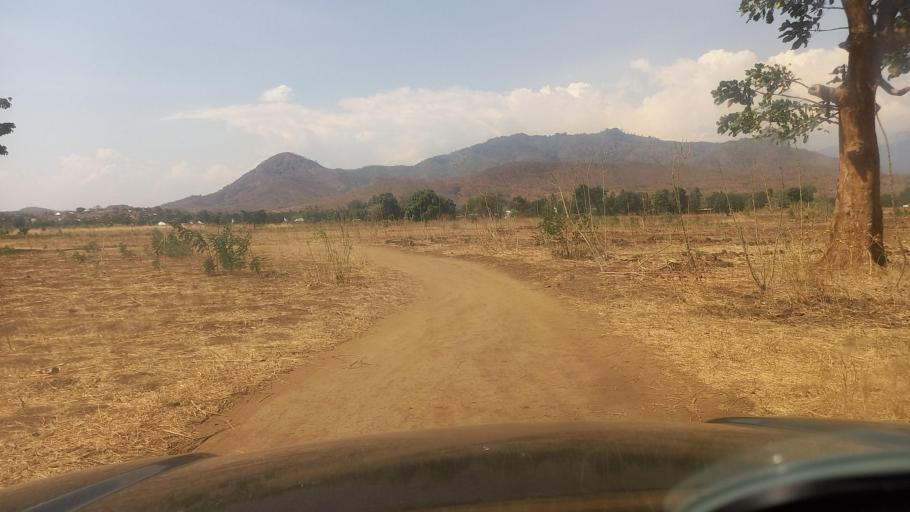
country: TZ
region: Morogoro
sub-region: Kilosa
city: Magole
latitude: -6.3287
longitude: 37.3821
